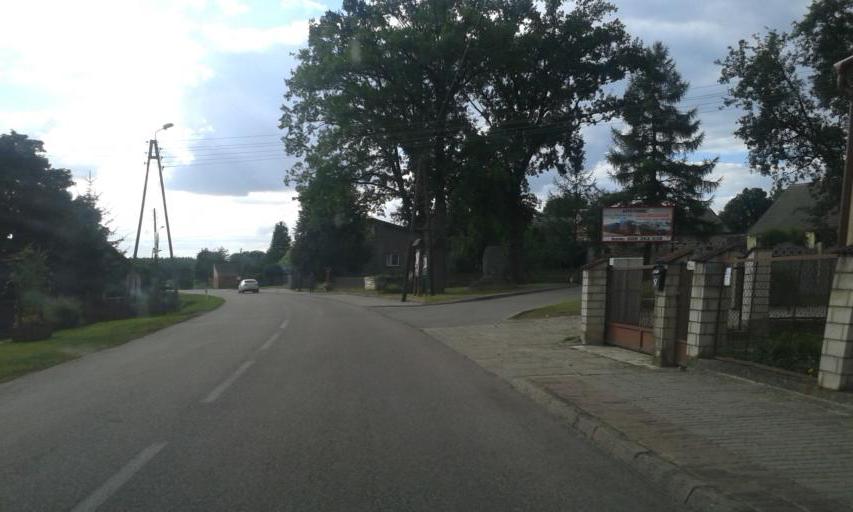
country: PL
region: West Pomeranian Voivodeship
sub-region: Powiat szczecinecki
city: Barwice
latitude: 53.7574
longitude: 16.2527
